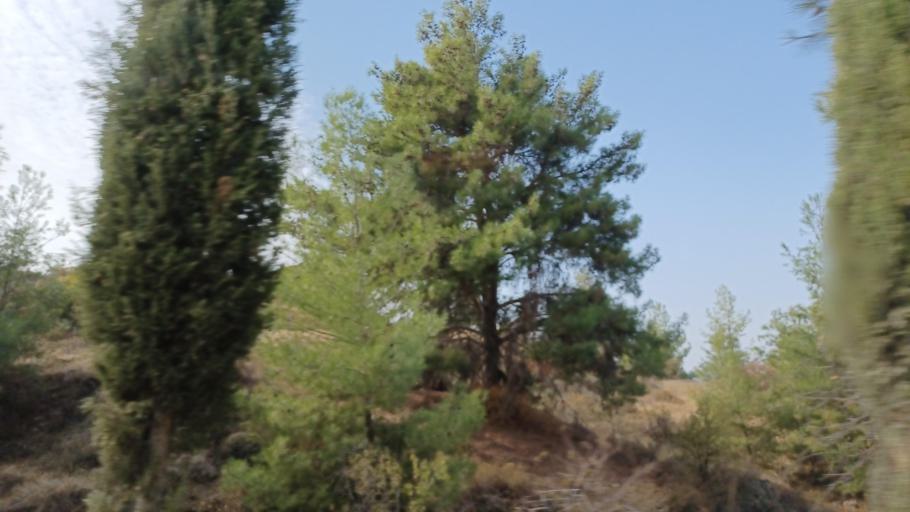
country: CY
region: Lefkosia
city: Kakopetria
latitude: 35.0351
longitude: 32.9020
